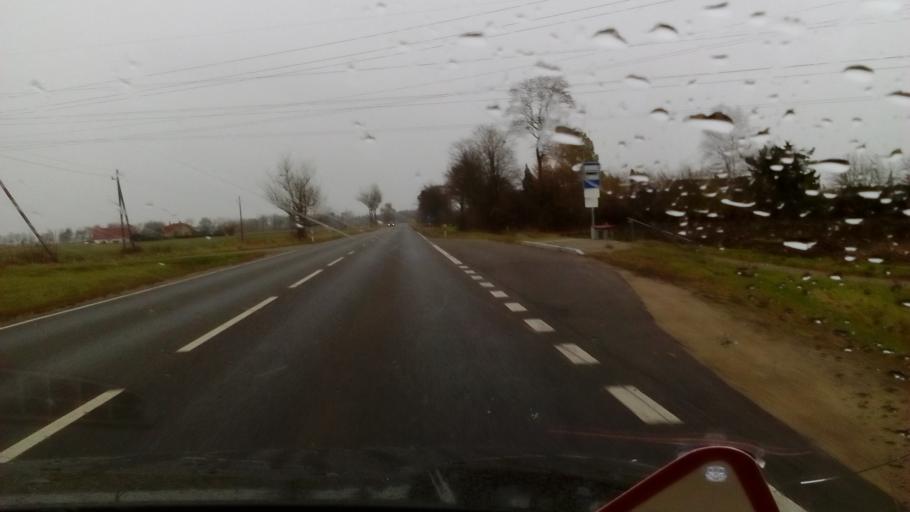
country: LT
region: Marijampoles apskritis
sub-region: Marijampole Municipality
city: Marijampole
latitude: 54.5510
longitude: 23.3944
